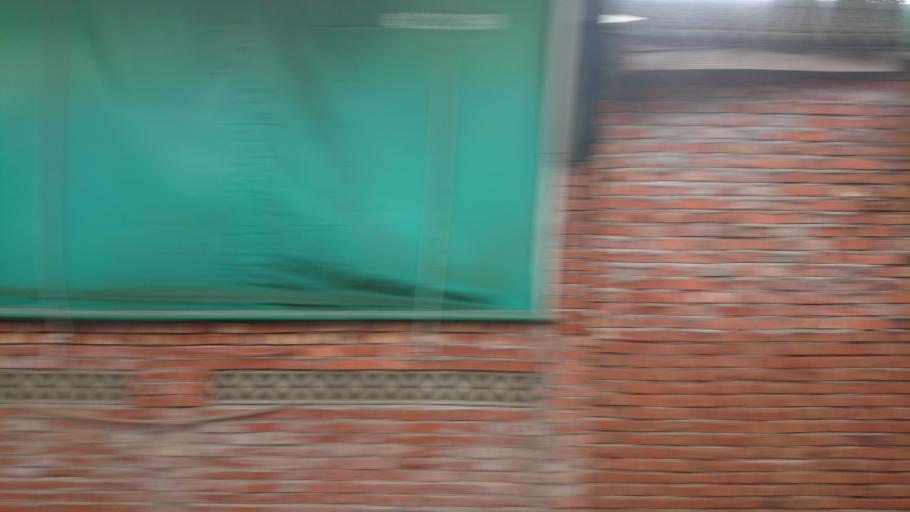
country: TW
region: Taiwan
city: Lugu
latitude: 23.8266
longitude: 120.7796
